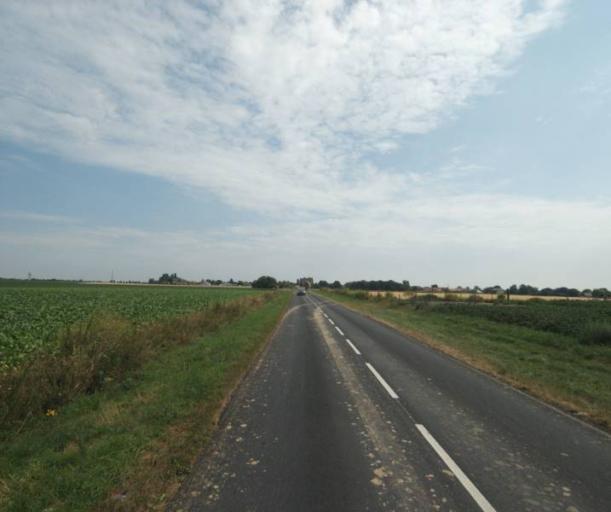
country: FR
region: Nord-Pas-de-Calais
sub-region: Departement du Nord
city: Sainghin-en-Weppes
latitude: 50.5646
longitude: 2.8849
